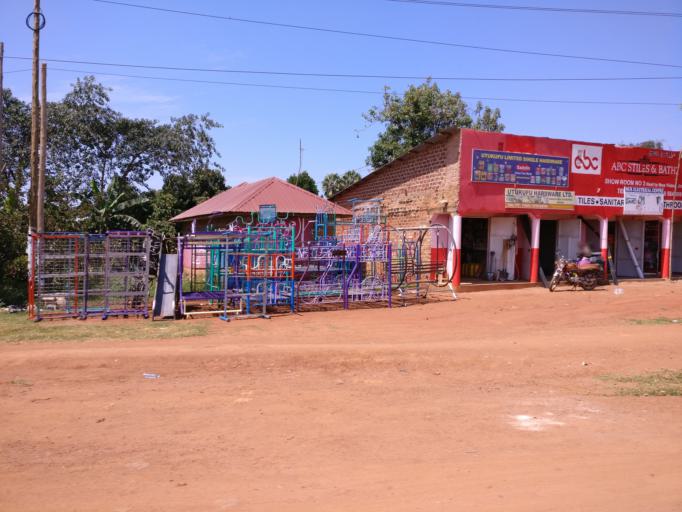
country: UG
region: Central Region
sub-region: Wakiso District
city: Entebbe
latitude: 0.1029
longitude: 32.5099
